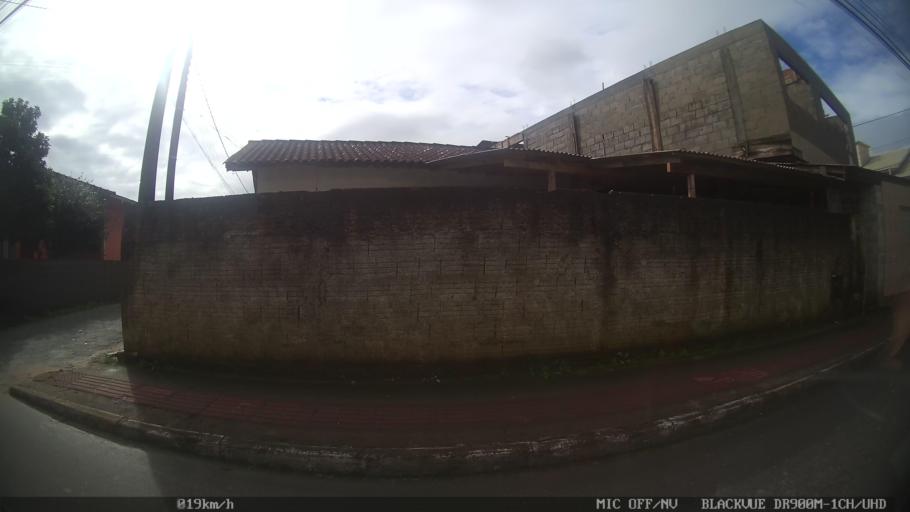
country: BR
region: Santa Catarina
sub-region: Biguacu
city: Biguacu
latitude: -27.5111
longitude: -48.6565
